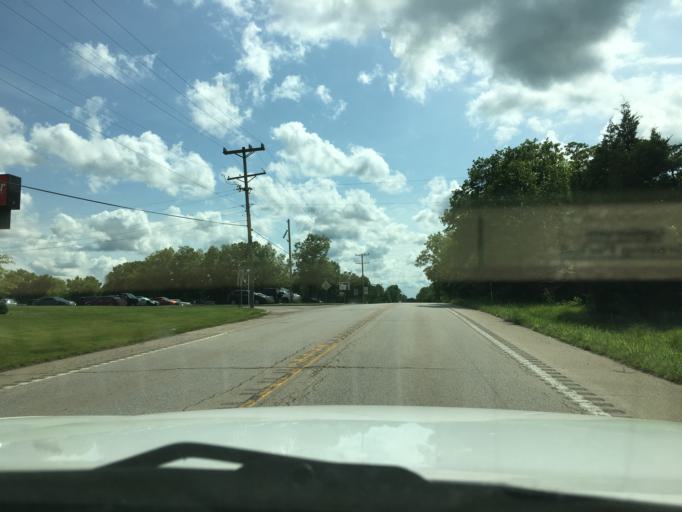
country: US
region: Missouri
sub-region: Franklin County
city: Gerald
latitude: 38.4087
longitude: -91.3192
